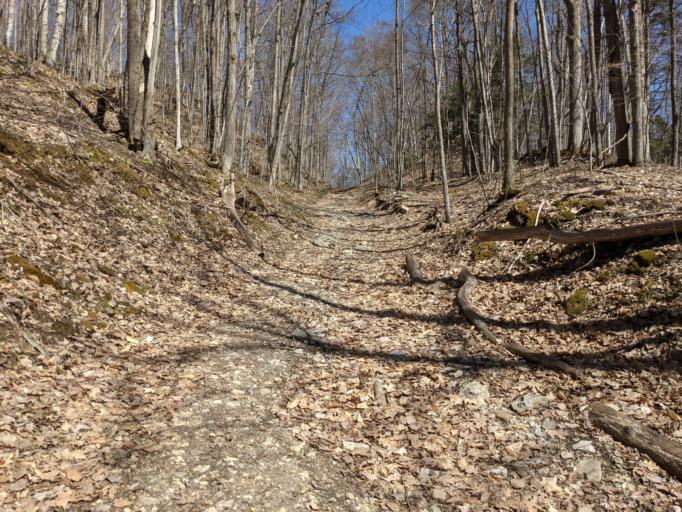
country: US
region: Vermont
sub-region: Bennington County
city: Manchester Center
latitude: 43.2418
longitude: -73.0137
